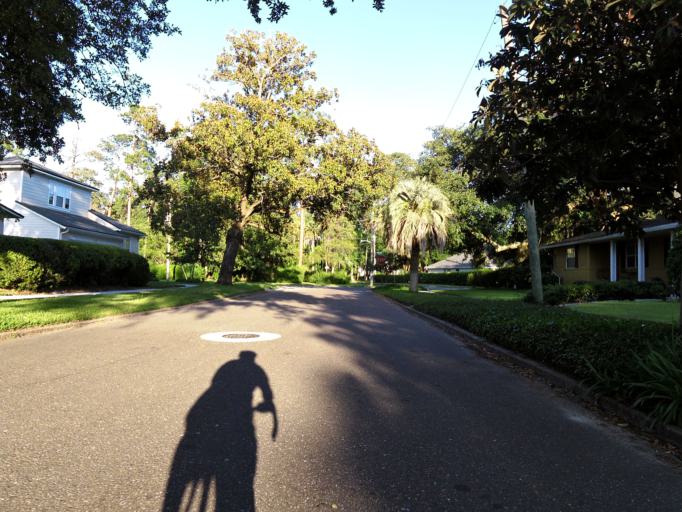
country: US
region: Florida
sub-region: Clay County
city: Orange Park
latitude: 30.2481
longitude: -81.6893
